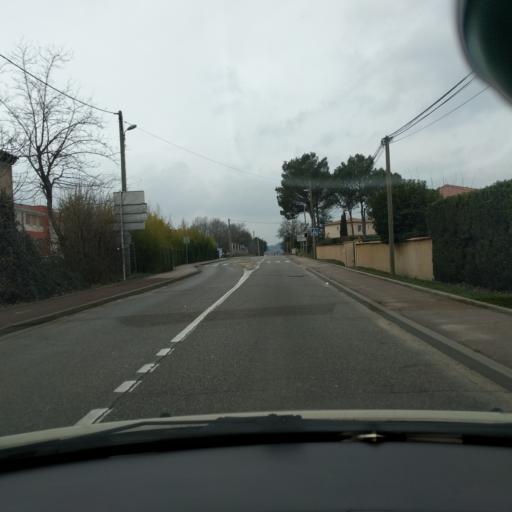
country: FR
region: Provence-Alpes-Cote d'Azur
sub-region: Departement des Bouches-du-Rhone
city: Fuveau
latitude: 43.4781
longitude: 5.5363
